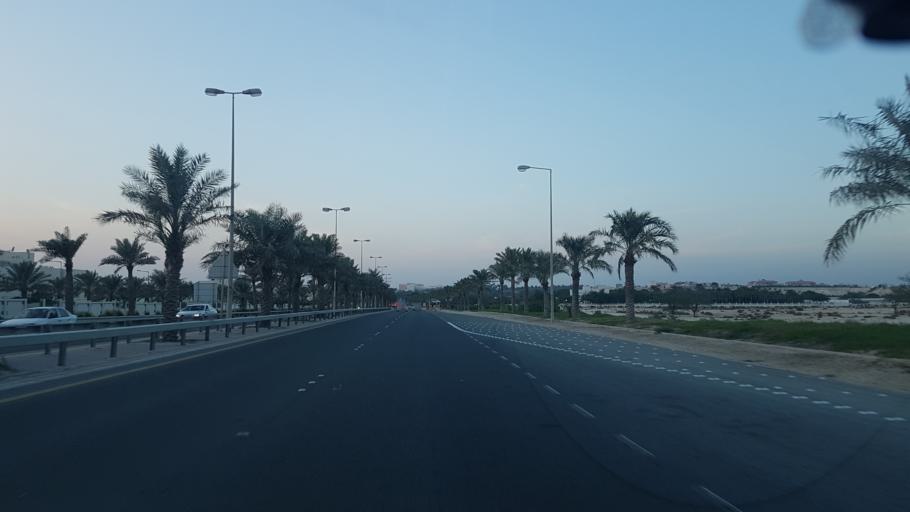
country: BH
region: Northern
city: Ar Rifa'
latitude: 26.1039
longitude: 50.5417
